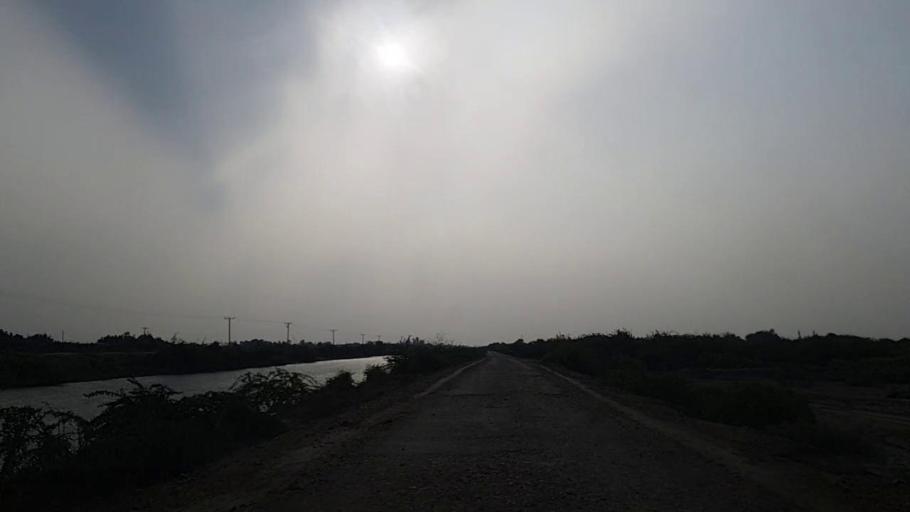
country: PK
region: Sindh
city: Mirpur Sakro
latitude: 24.6158
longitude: 67.5445
